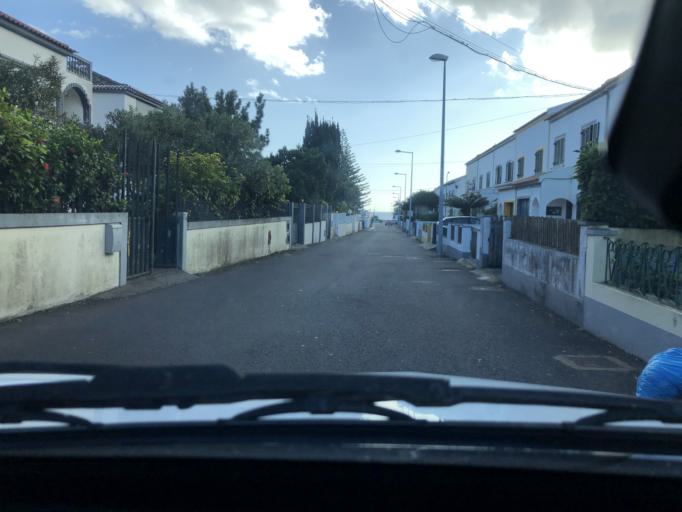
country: PT
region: Azores
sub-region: Ponta Delgada
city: Rosto de Cao
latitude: 37.7477
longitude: -25.6547
